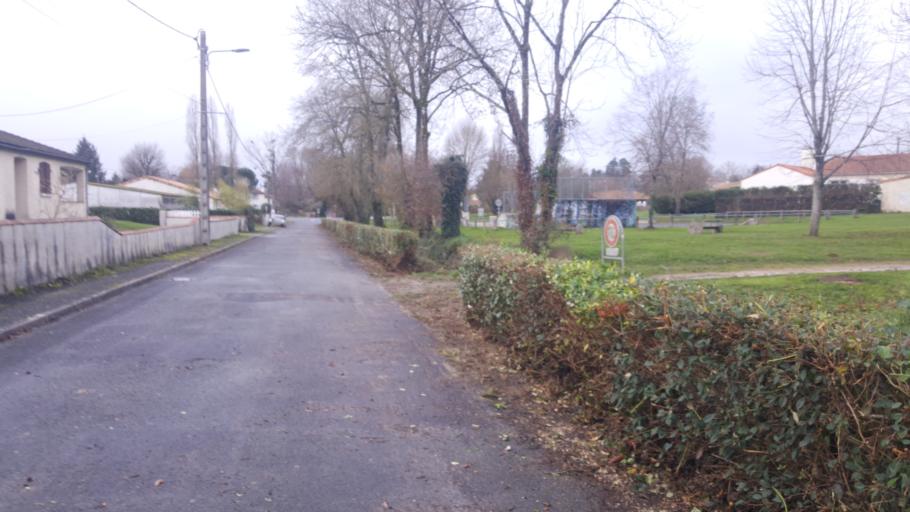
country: FR
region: Poitou-Charentes
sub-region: Departement des Deux-Sevres
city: Melle
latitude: 46.2256
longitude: -0.1351
